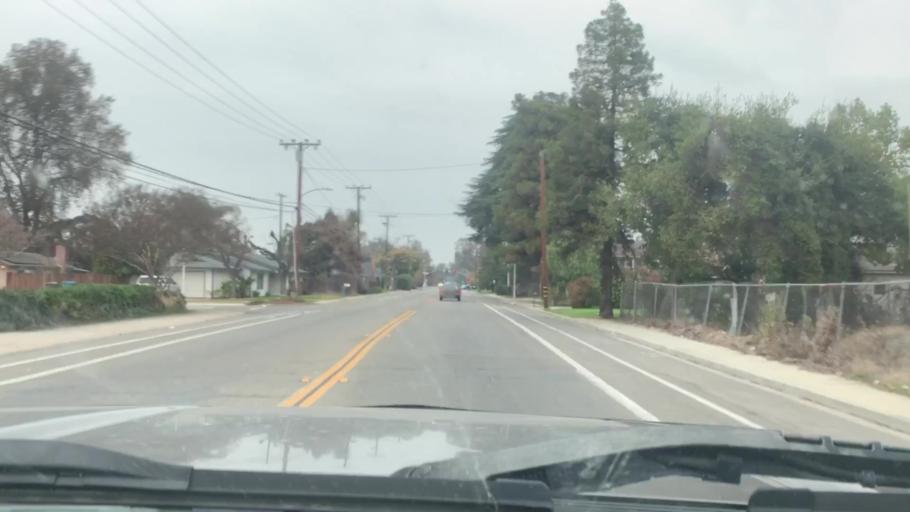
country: US
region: California
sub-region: Tulare County
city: Visalia
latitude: 36.3172
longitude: -119.3054
